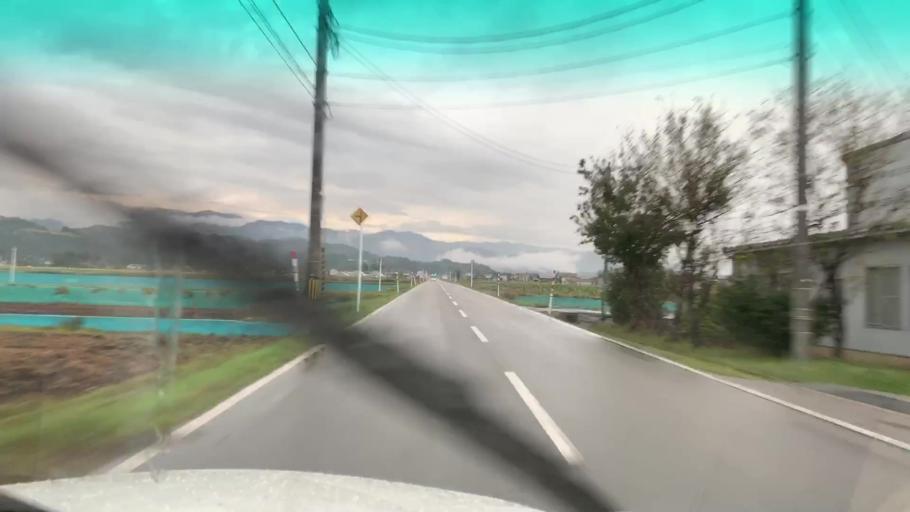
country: JP
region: Toyama
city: Kamiichi
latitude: 36.6384
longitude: 137.3283
